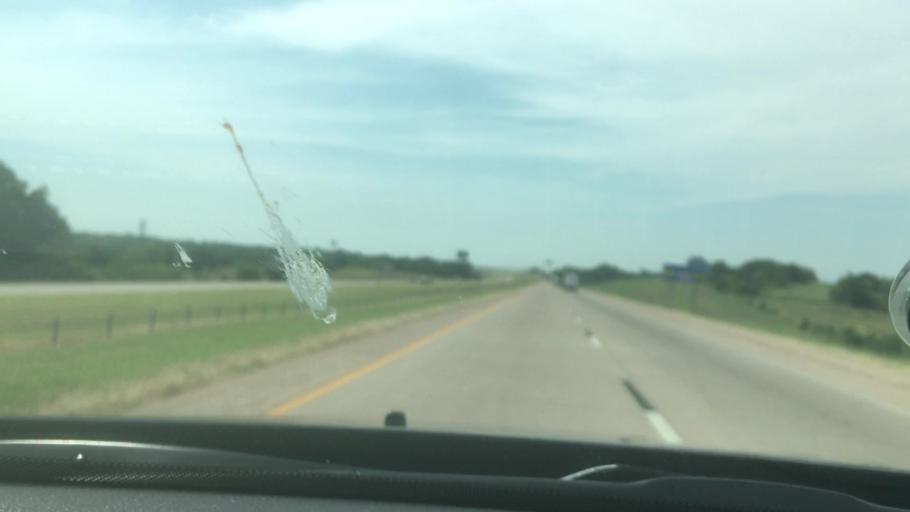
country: US
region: Oklahoma
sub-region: Garvin County
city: Pauls Valley
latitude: 34.7219
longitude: -97.2530
